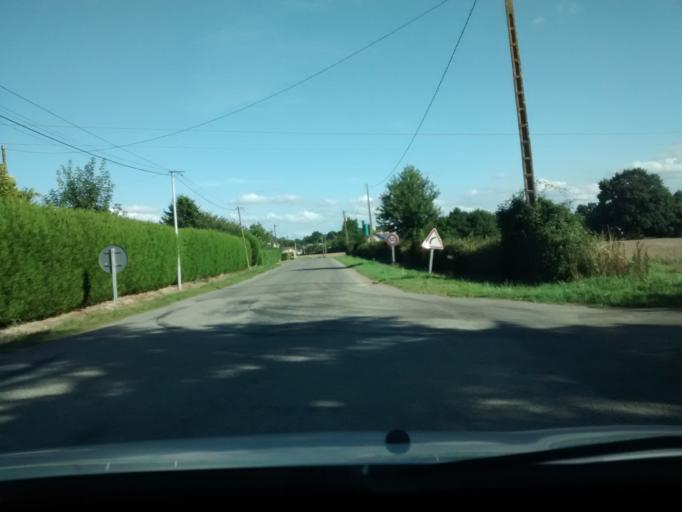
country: FR
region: Brittany
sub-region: Departement d'Ille-et-Vilaine
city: Nouvoitou
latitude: 48.0716
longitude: -1.5684
